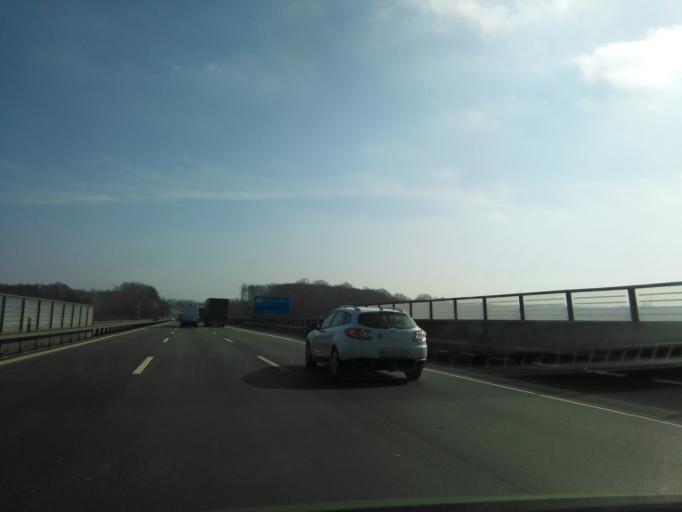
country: DK
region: South Denmark
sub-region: Middelfart Kommune
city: Strib
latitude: 55.5169
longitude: 9.7577
